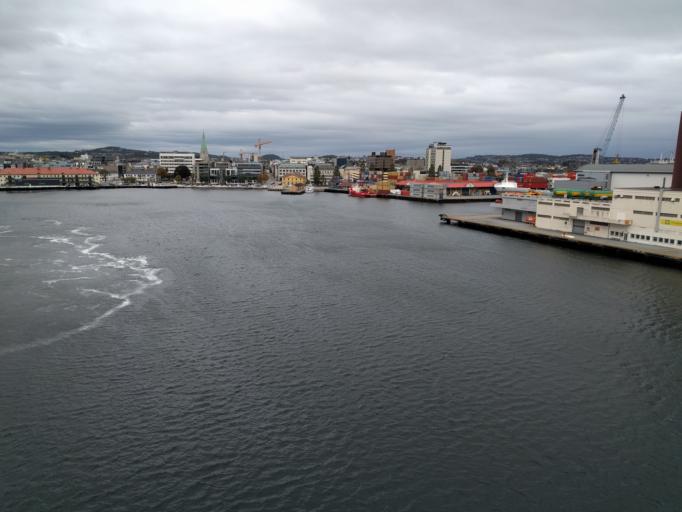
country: NO
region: Vest-Agder
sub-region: Kristiansand
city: Kristiansand
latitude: 58.1402
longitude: 7.9865
